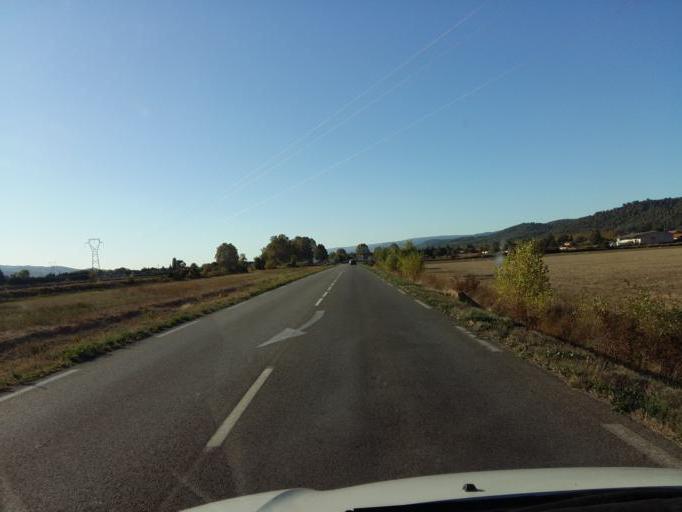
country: FR
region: Provence-Alpes-Cote d'Azur
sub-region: Departement du Vaucluse
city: Villelaure
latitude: 43.7052
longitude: 5.4358
